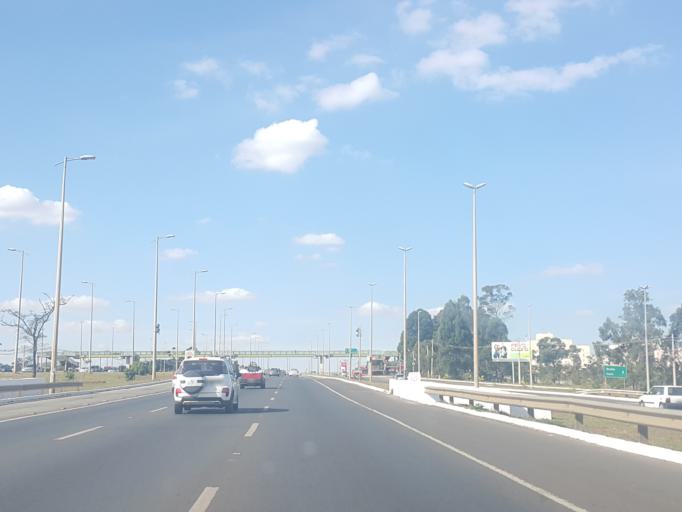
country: BR
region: Federal District
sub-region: Brasilia
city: Brasilia
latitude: -15.8131
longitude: -48.0000
